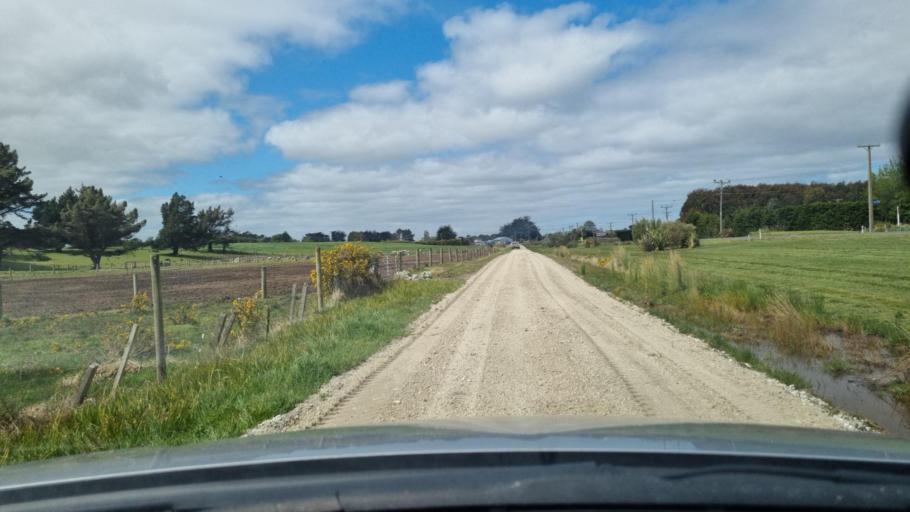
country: NZ
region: Southland
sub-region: Invercargill City
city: Invercargill
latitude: -46.4424
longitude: 168.3935
